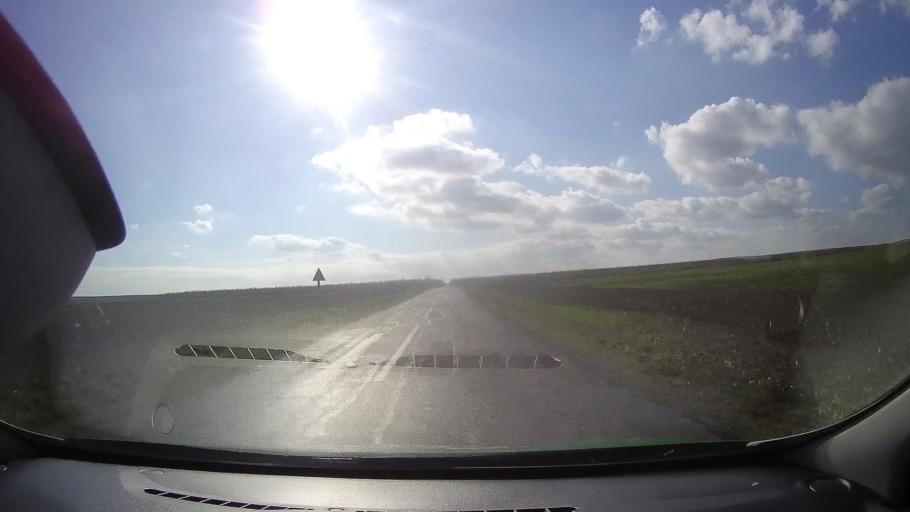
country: RO
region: Constanta
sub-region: Comuna Mihai Viteazu
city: Mihai Viteazu
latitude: 44.6186
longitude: 28.7264
